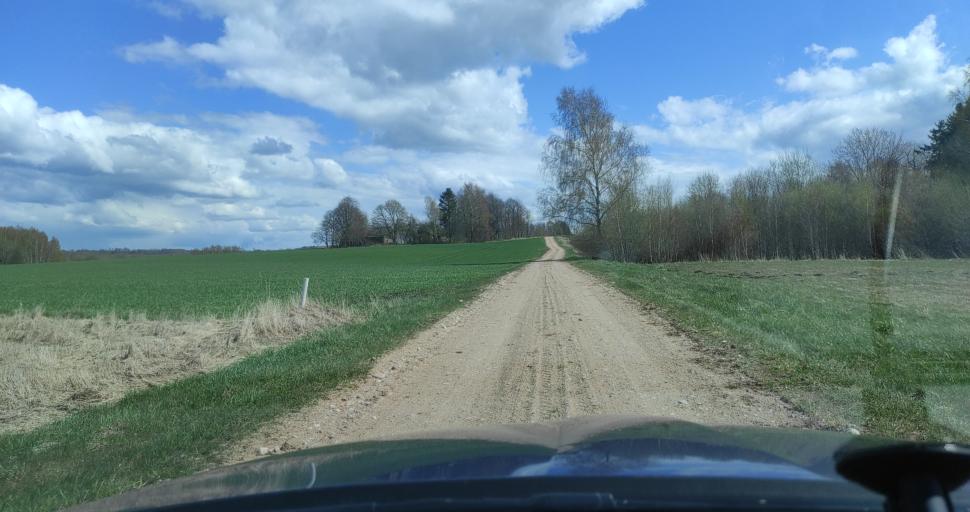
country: LV
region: Kuldigas Rajons
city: Kuldiga
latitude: 56.8693
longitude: 21.7951
